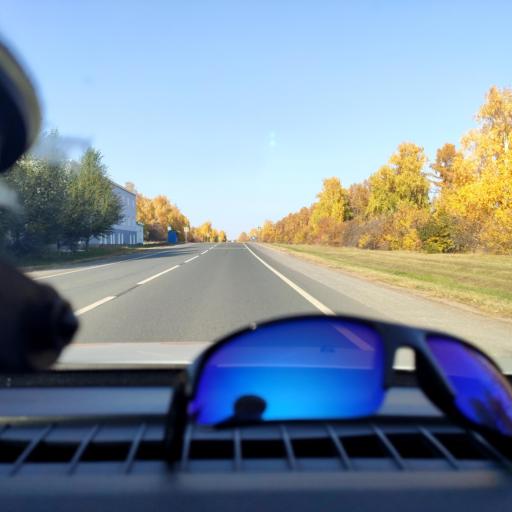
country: RU
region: Samara
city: Volzhskiy
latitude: 53.4544
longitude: 50.1263
